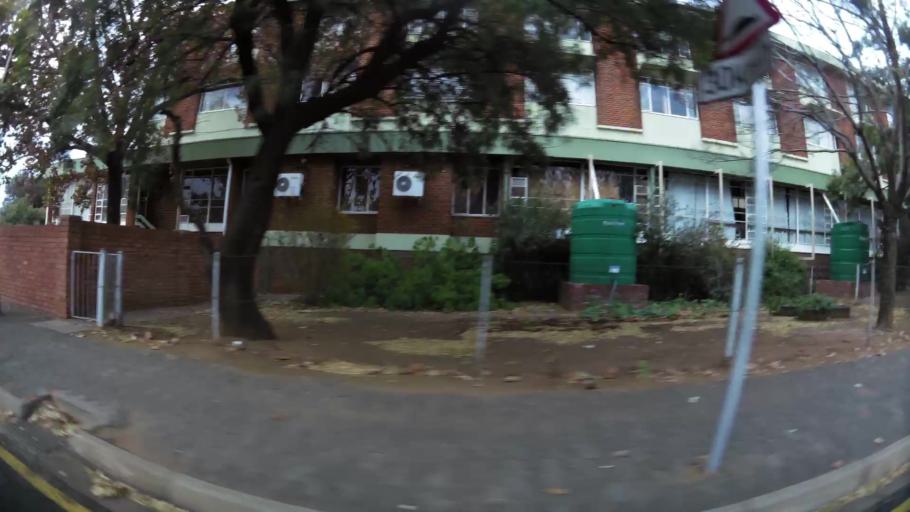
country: ZA
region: Orange Free State
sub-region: Mangaung Metropolitan Municipality
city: Bloemfontein
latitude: -29.1082
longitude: 26.1898
